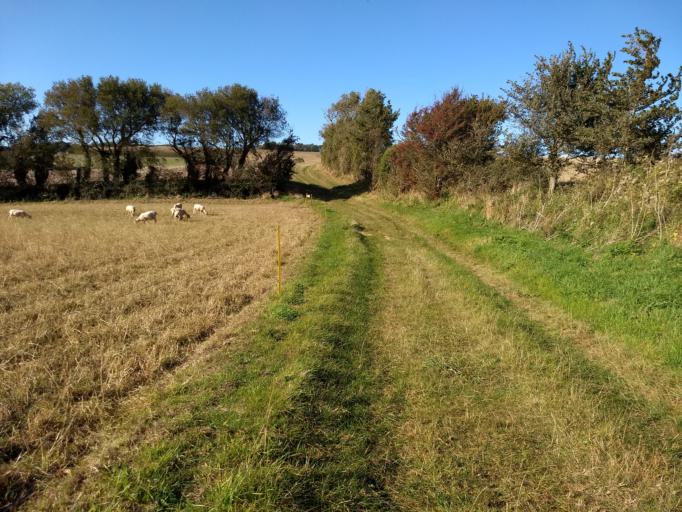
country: GB
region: England
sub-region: Isle of Wight
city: Newport
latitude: 50.6492
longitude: -1.2876
